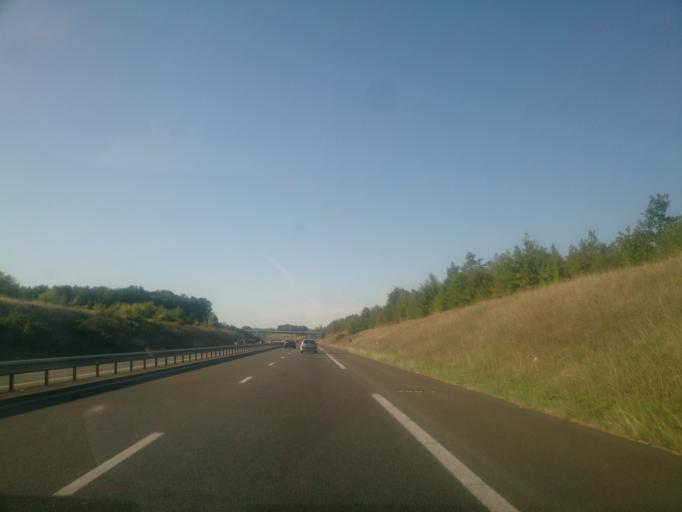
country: FR
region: Midi-Pyrenees
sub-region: Departement du Tarn-et-Garonne
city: Caussade
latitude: 44.2164
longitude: 1.5402
